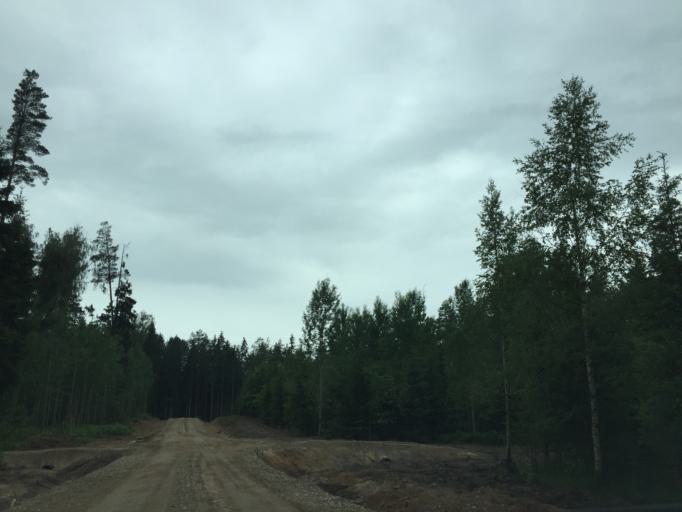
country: LV
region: Tukuma Rajons
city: Tukums
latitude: 57.0048
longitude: 23.1127
